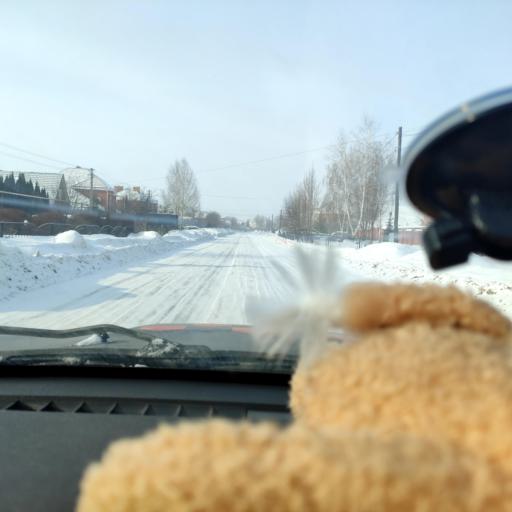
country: RU
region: Samara
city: Podstepki
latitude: 53.5108
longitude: 49.1378
